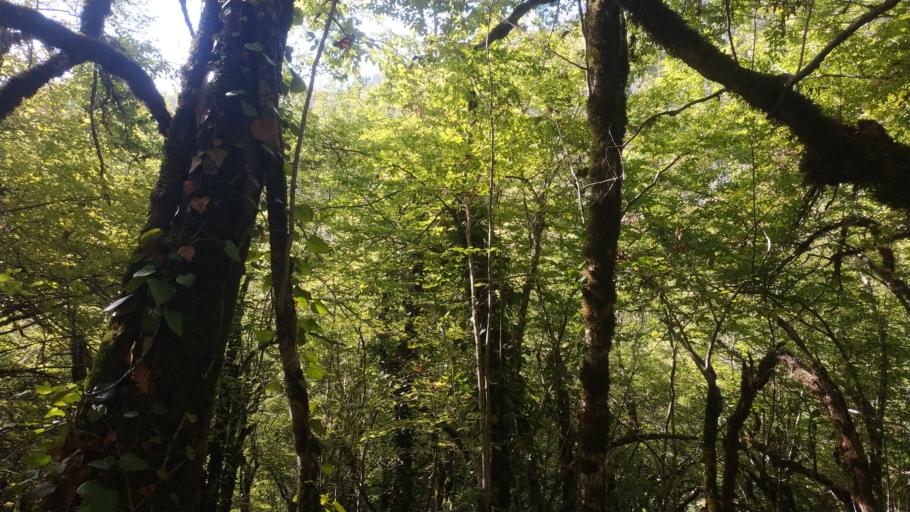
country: RU
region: Krasnodarskiy
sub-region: Sochi City
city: Lazarevskoye
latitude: 43.9841
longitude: 39.4077
